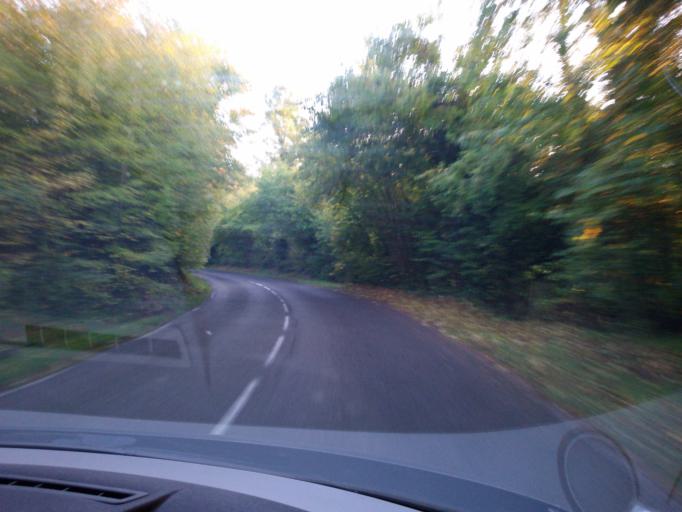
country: FR
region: Lower Normandy
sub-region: Departement du Calvados
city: Ablon
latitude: 49.4271
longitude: 0.3387
